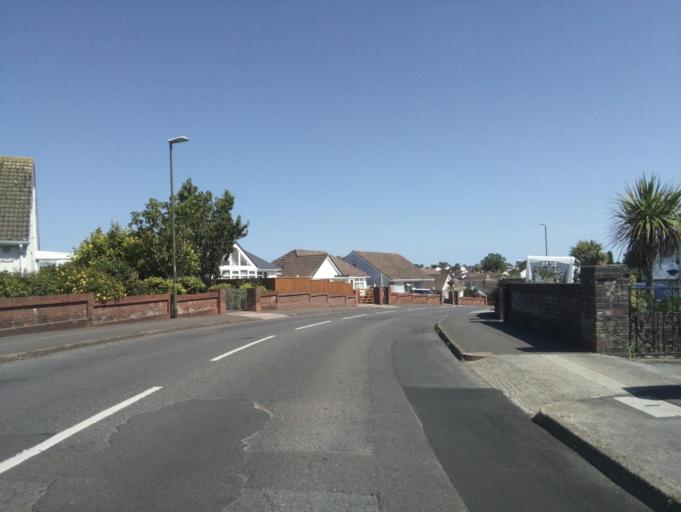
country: GB
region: England
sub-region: Borough of Torbay
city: Paignton
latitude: 50.4150
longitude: -3.5742
